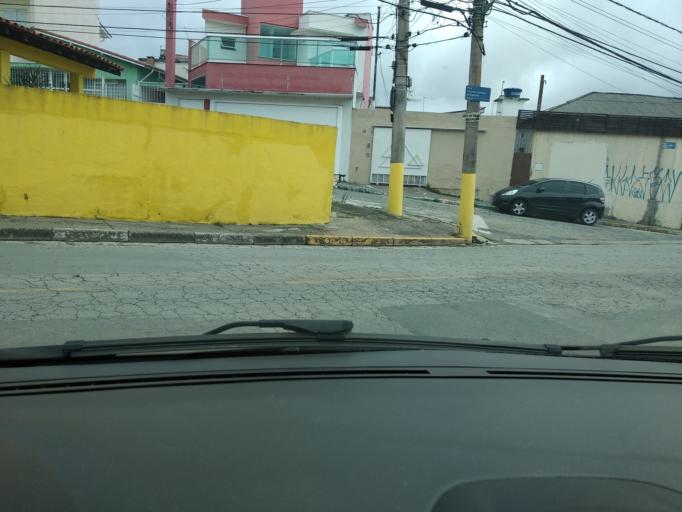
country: BR
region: Sao Paulo
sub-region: Mogi das Cruzes
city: Mogi das Cruzes
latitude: -23.5314
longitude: -46.1784
